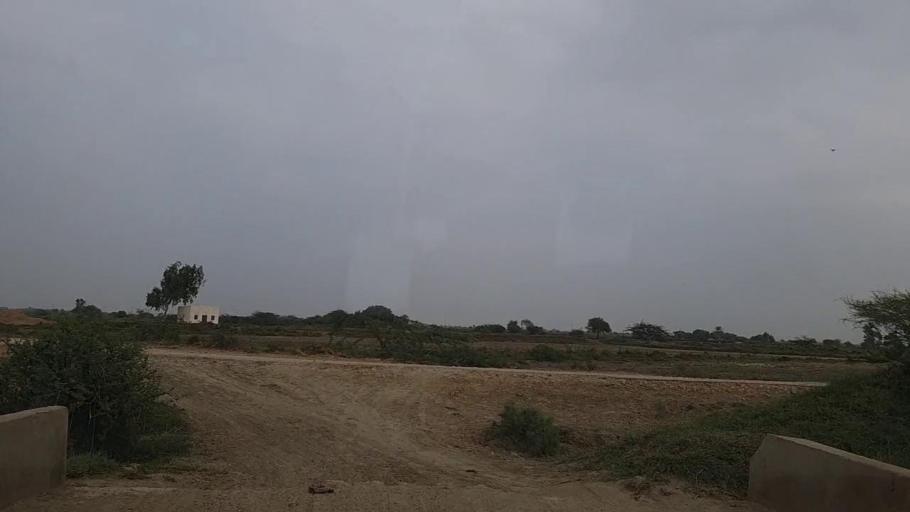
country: PK
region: Sindh
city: Mirpur Sakro
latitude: 24.5961
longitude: 67.6968
